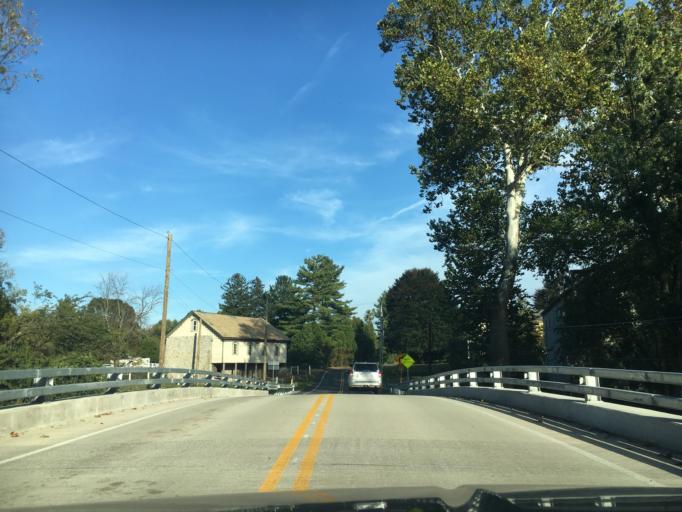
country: US
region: Pennsylvania
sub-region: Lancaster County
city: Brownstown
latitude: 40.1279
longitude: -76.2000
